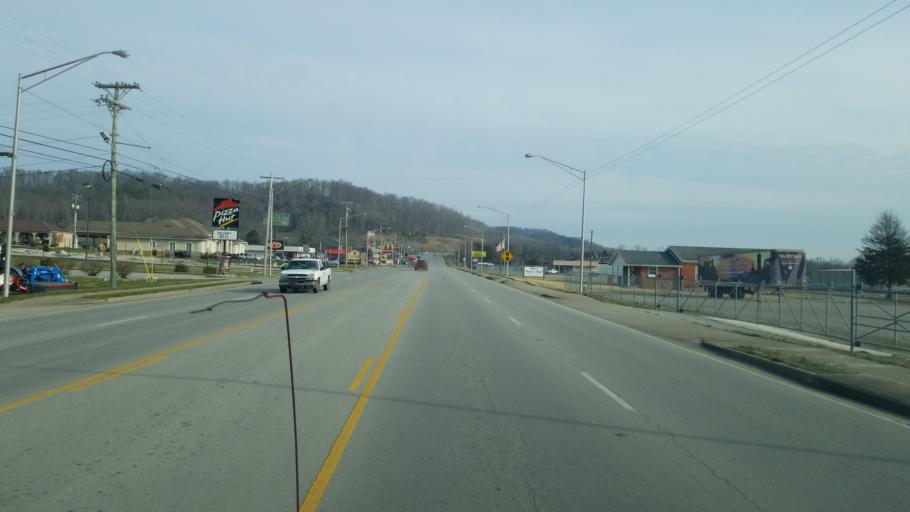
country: US
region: Kentucky
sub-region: Casey County
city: Liberty
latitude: 37.3210
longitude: -84.9269
